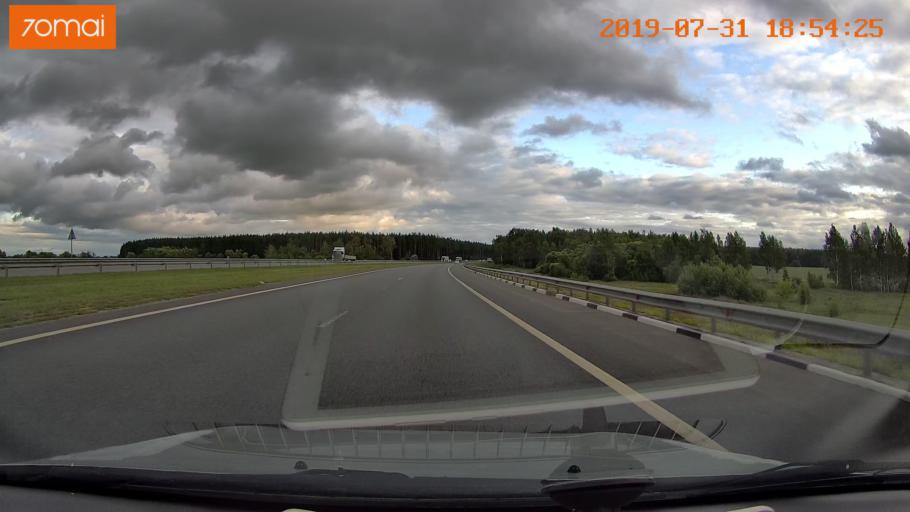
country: RU
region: Moskovskaya
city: Raduzhnyy
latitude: 55.1904
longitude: 38.6681
